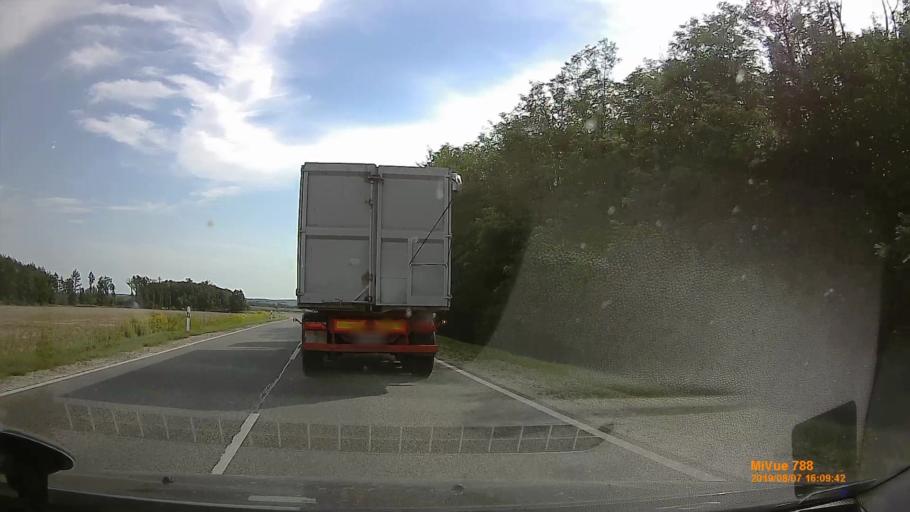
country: HU
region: Zala
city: Zalalovo
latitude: 46.8897
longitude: 16.6010
